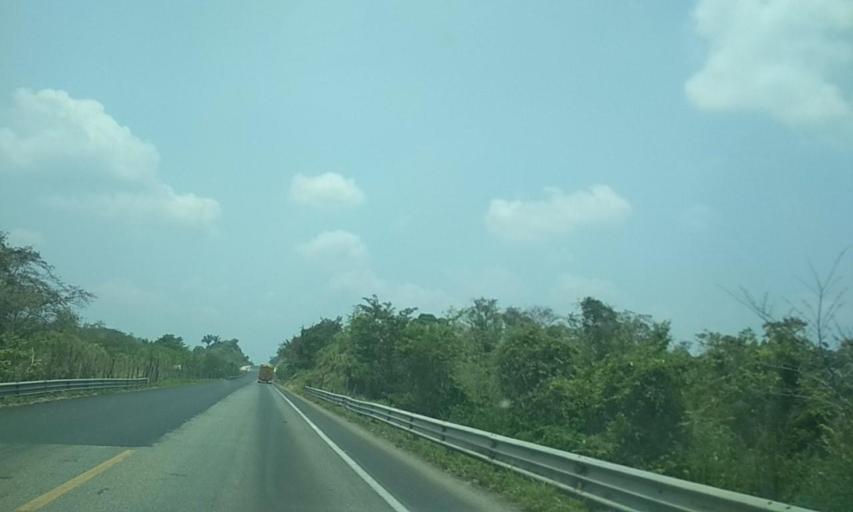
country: MX
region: Tabasco
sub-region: Huimanguillo
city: Francisco Rueda
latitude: 17.7234
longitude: -93.9578
